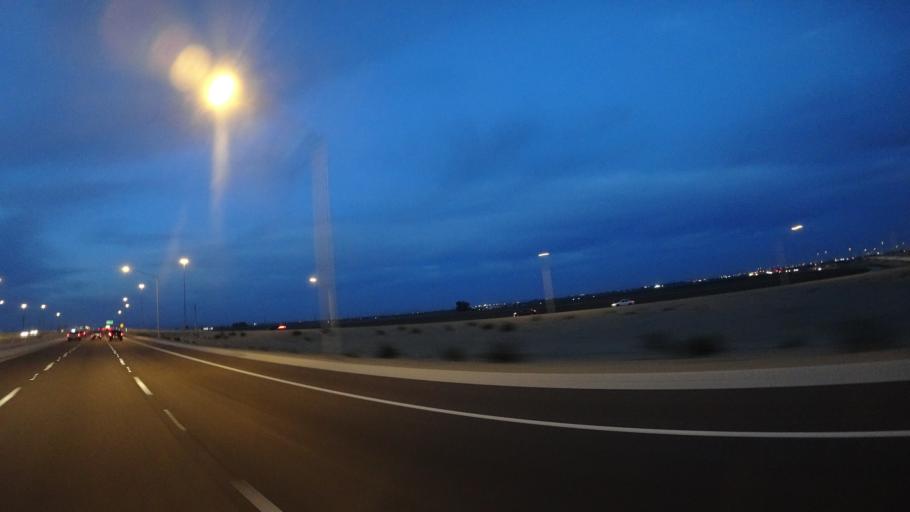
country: US
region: Arizona
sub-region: Maricopa County
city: Citrus Park
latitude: 33.5612
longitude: -112.4180
